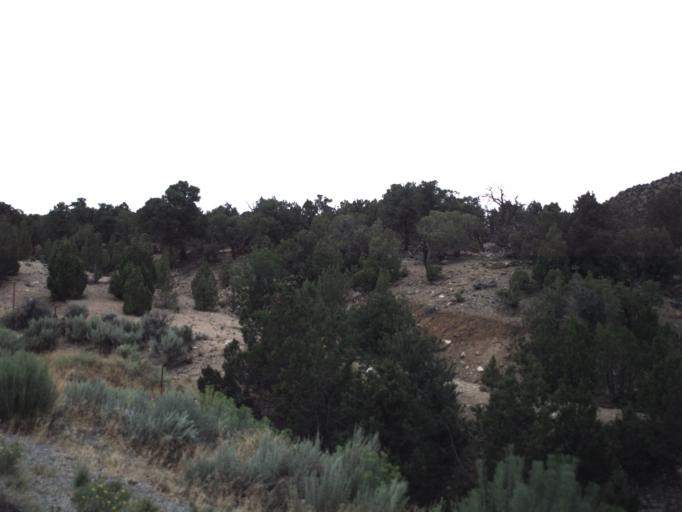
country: US
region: Utah
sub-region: Carbon County
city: East Carbon City
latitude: 39.4544
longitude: -110.3828
